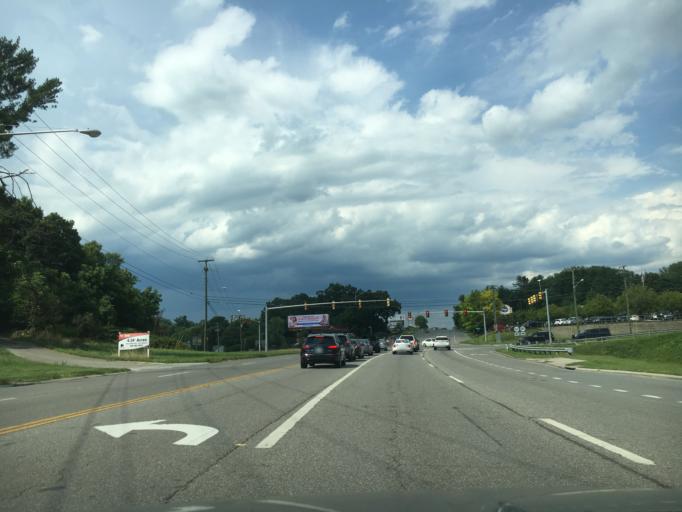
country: US
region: Virginia
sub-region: Roanoke County
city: Cave Spring
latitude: 37.2232
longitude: -80.0139
